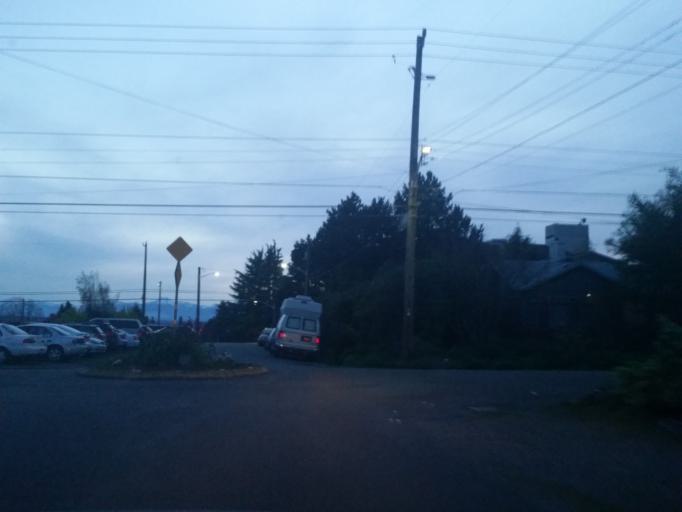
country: US
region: Washington
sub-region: King County
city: Shoreline
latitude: 47.7106
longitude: -122.3539
